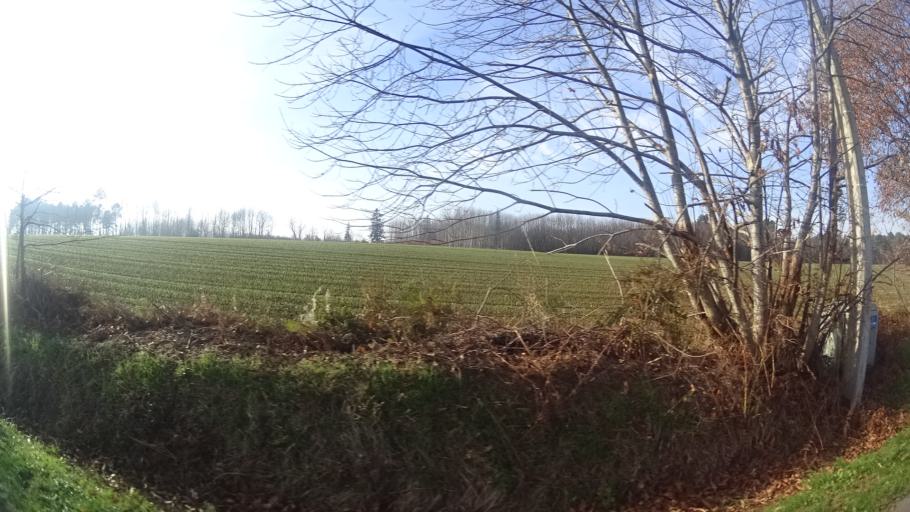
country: FR
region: Brittany
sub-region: Departement du Morbihan
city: Allaire
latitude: 47.6167
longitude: -2.1488
